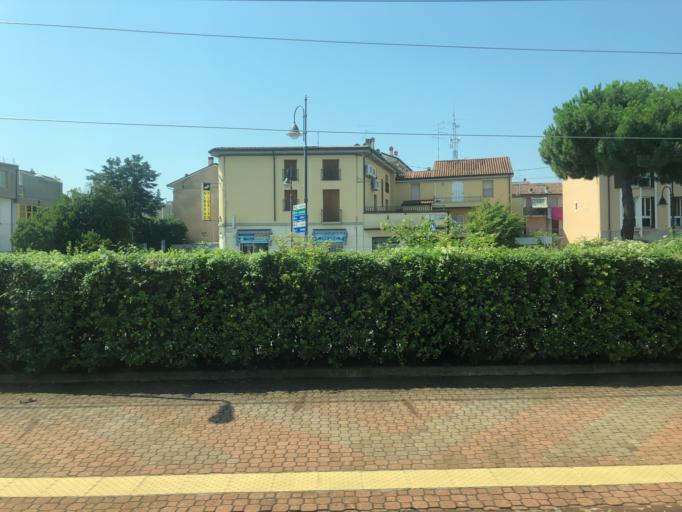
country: IT
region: Emilia-Romagna
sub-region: Forli-Cesena
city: Cesena
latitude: 44.1447
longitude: 12.2520
